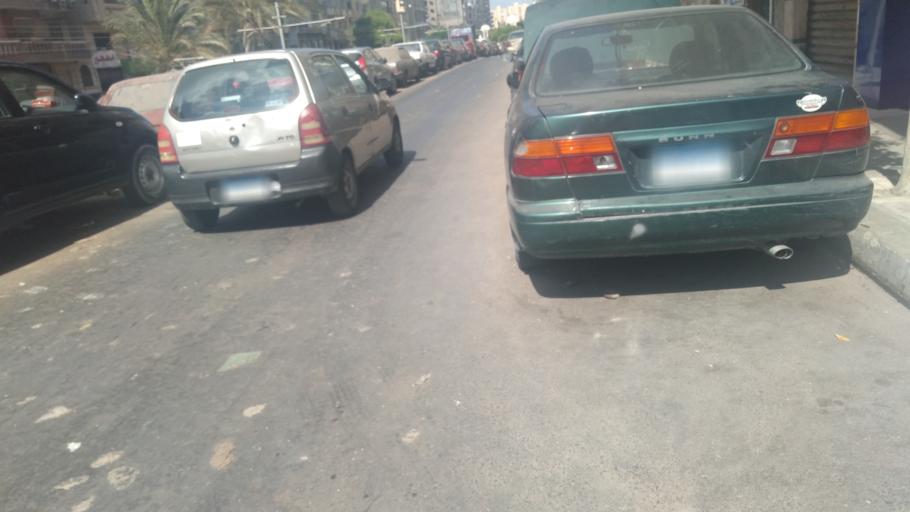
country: EG
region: Alexandria
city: Alexandria
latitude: 31.2202
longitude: 29.9360
